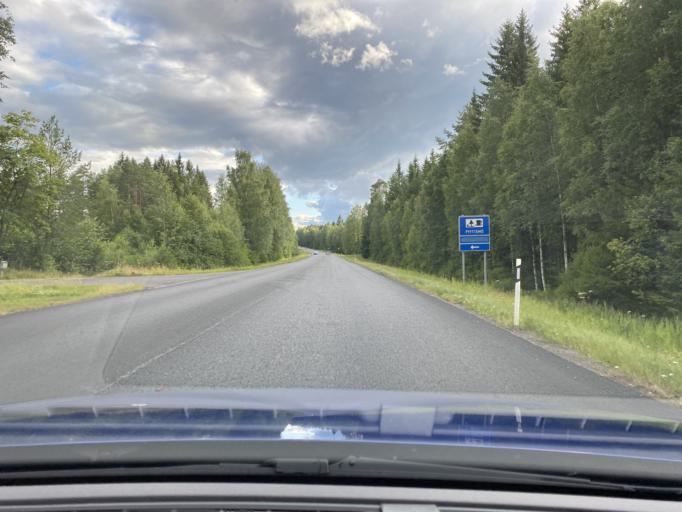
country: FI
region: Haeme
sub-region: Haemeenlinna
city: Renko
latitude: 60.9254
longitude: 24.3437
